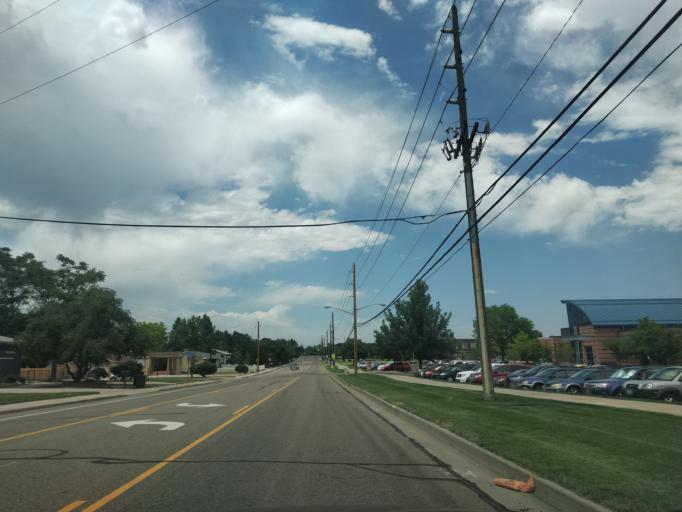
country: US
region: Colorado
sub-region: Jefferson County
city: Lakewood
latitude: 39.6771
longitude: -105.1097
